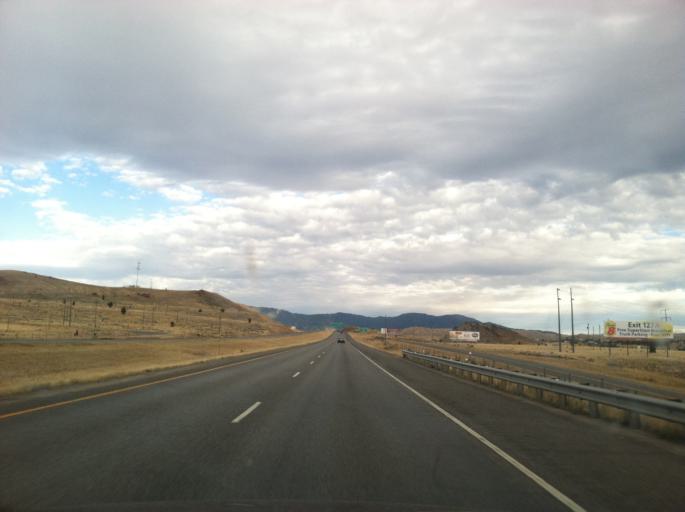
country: US
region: Montana
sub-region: Silver Bow County
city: Butte-Silver Bow (Balance)
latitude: 46.0078
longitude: -112.6649
